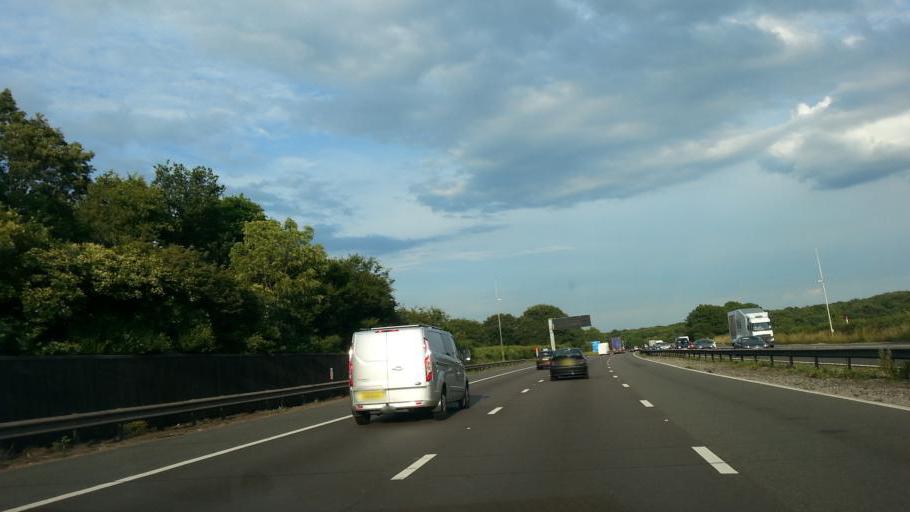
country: GB
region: England
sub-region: Solihull
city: Tidbury Green
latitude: 52.3542
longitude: -1.8748
